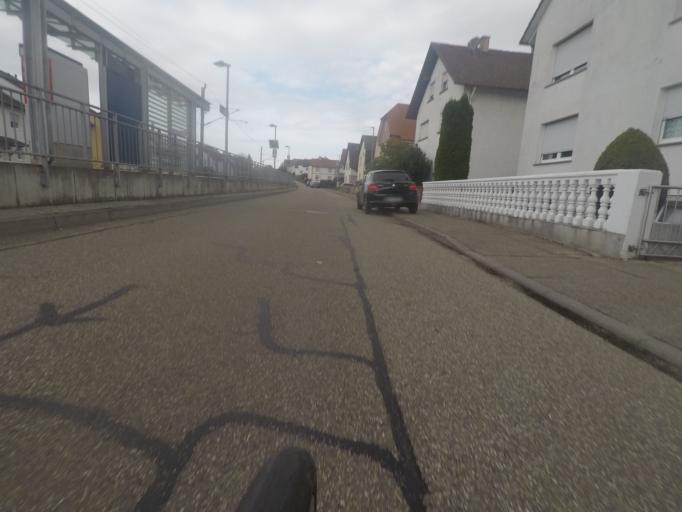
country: DE
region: Baden-Wuerttemberg
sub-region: Karlsruhe Region
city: Gaggenau
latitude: 48.7931
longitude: 8.3381
